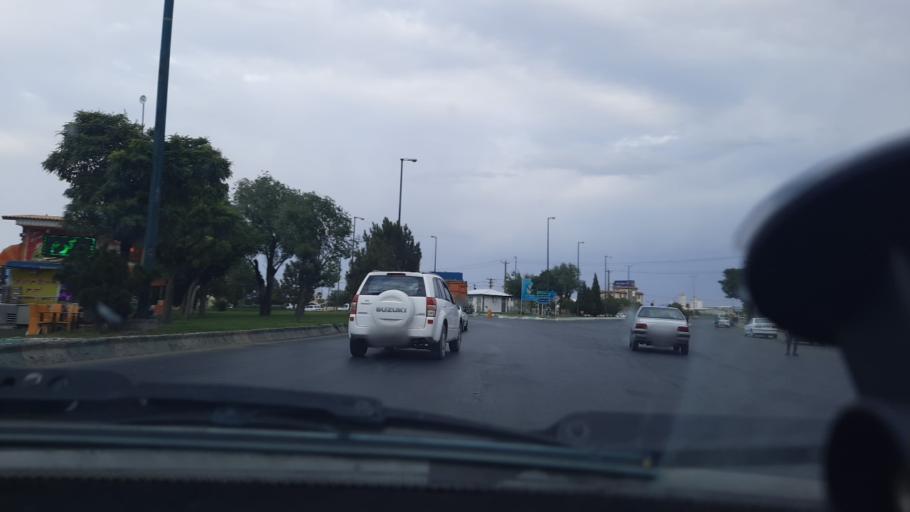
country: IR
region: Markazi
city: Arak
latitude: 34.0711
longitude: 49.7768
